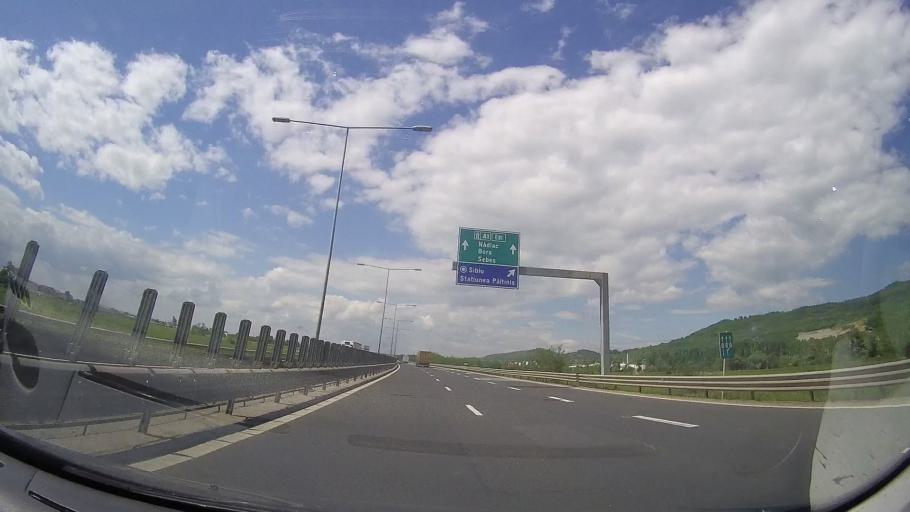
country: RO
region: Sibiu
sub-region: Comuna Selimbar
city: Selimbar
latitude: 45.7962
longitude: 24.1946
